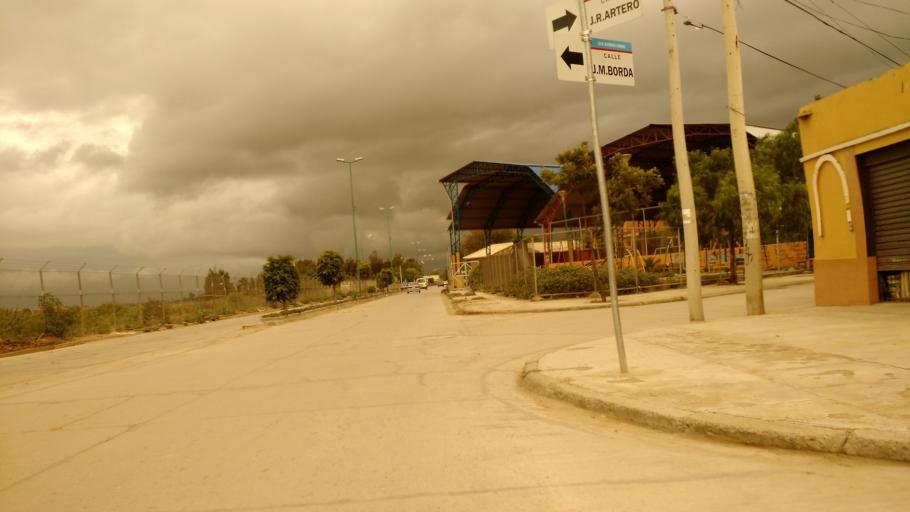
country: BO
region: Cochabamba
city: Cochabamba
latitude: -17.4288
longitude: -66.1636
